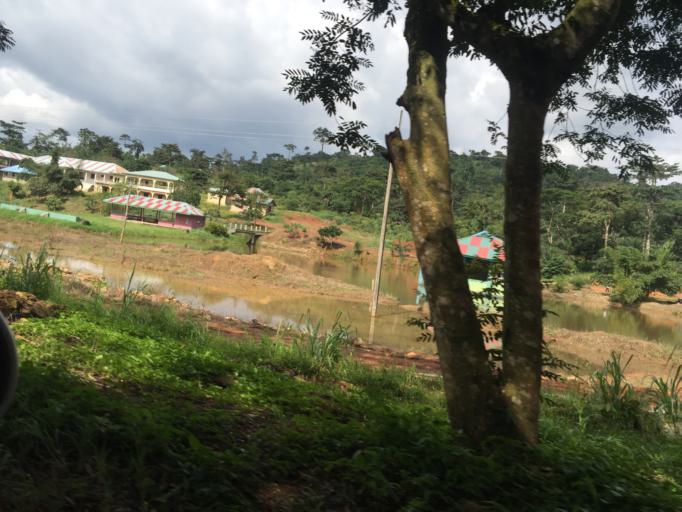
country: GH
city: Mpraeso
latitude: 6.6082
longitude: -0.7399
